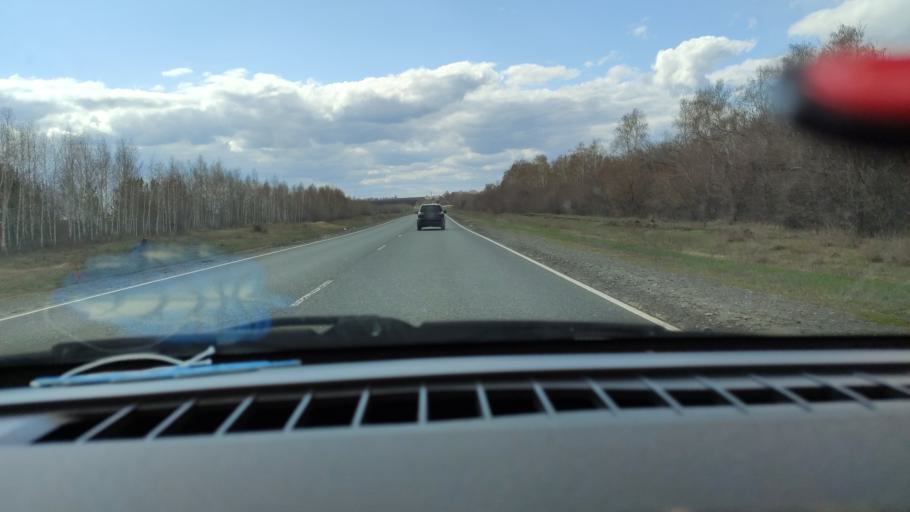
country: RU
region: Saratov
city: Balakovo
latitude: 52.1392
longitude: 47.7993
